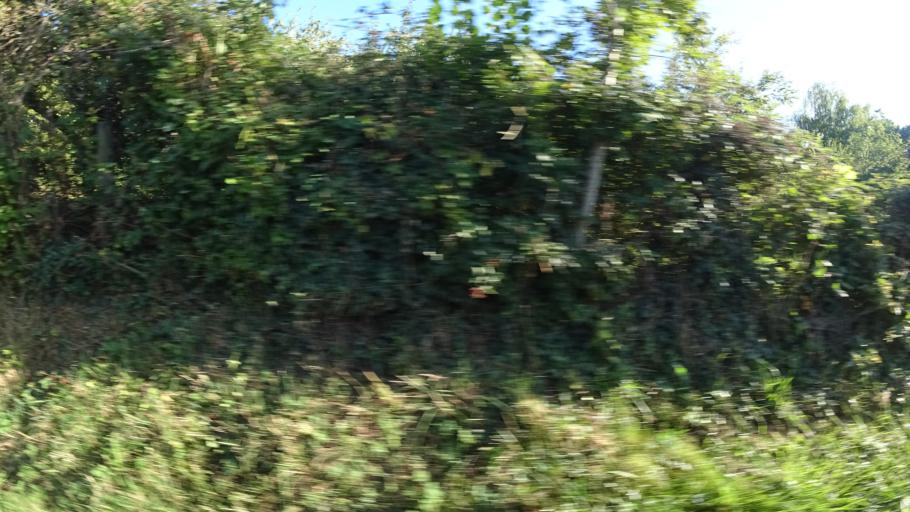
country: FR
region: Midi-Pyrenees
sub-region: Departement de l'Aveyron
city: Firmi
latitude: 44.5292
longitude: 2.3158
